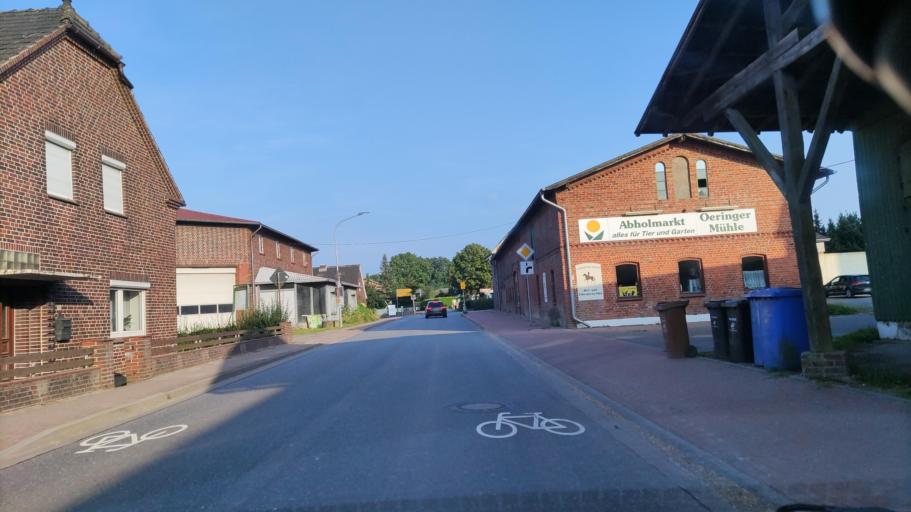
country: DE
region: Schleswig-Holstein
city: Stuvenborn
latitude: 53.8290
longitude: 10.1437
